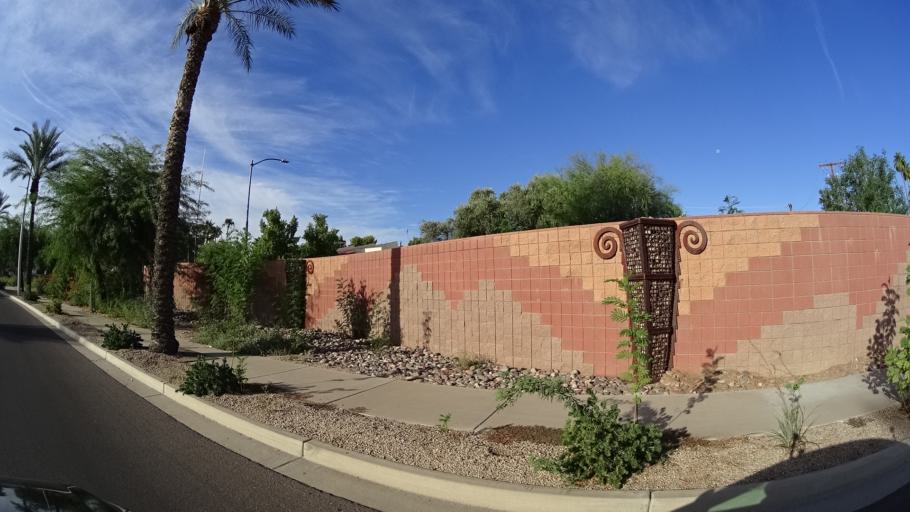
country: US
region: Arizona
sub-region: Maricopa County
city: Scottsdale
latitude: 33.4909
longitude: -111.9304
